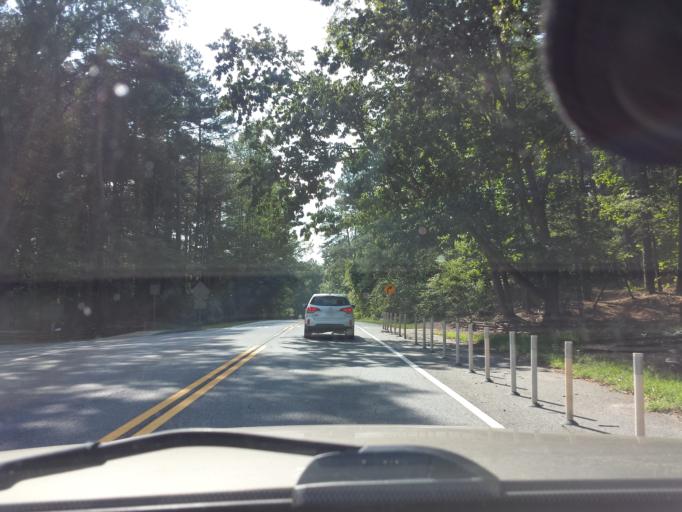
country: US
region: Georgia
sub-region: Cobb County
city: Marietta
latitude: 33.9456
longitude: -84.5968
